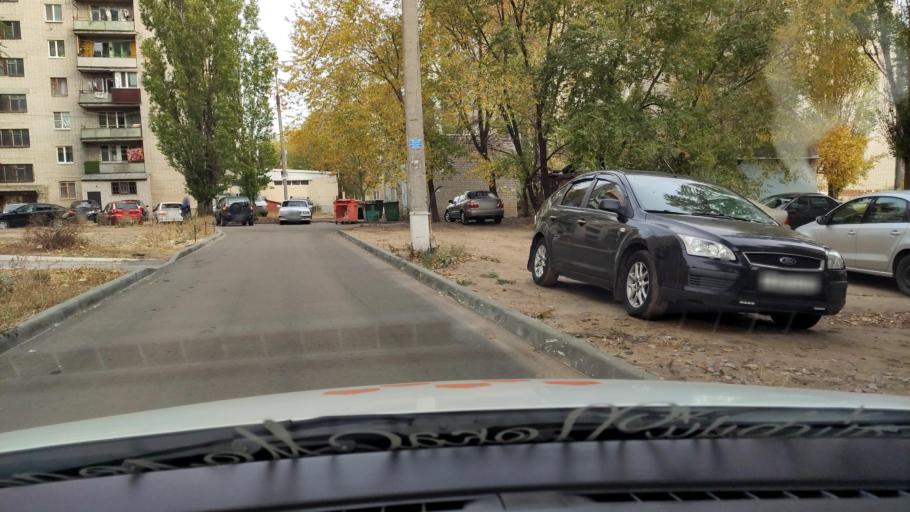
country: RU
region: Voronezj
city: Voronezh
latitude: 51.6382
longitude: 39.1565
